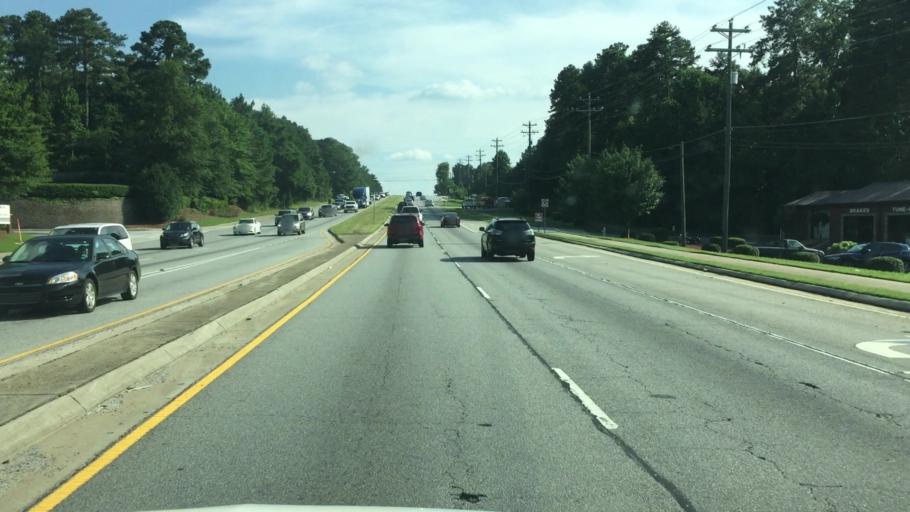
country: US
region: Georgia
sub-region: Gwinnett County
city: Snellville
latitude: 33.8974
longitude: -84.0065
